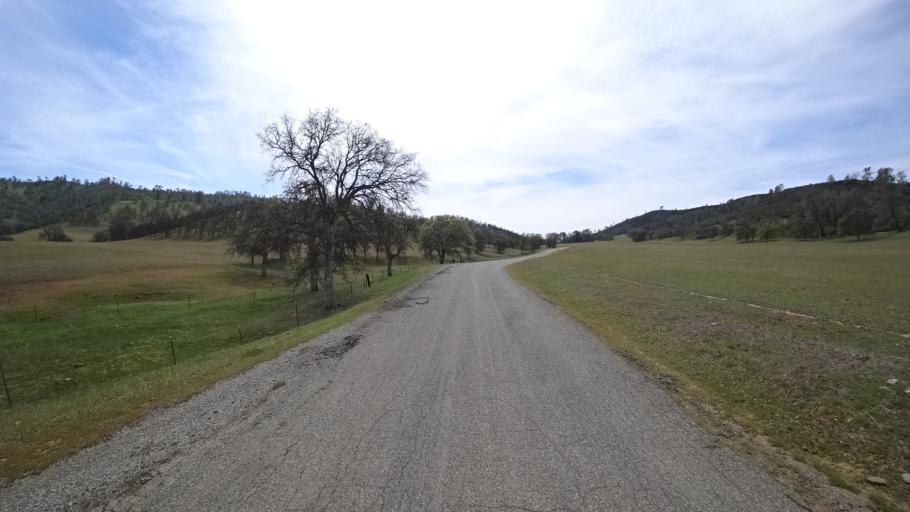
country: US
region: California
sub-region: Glenn County
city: Willows
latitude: 39.6072
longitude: -122.5263
